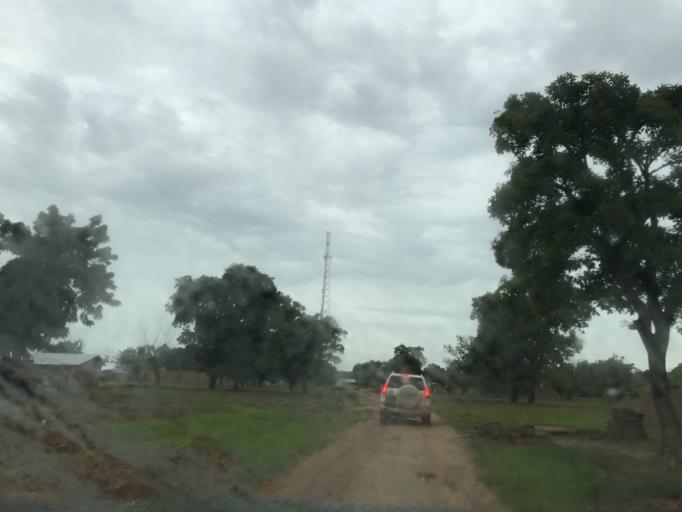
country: GH
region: Upper West
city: Wa
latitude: 10.5131
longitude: -2.6990
